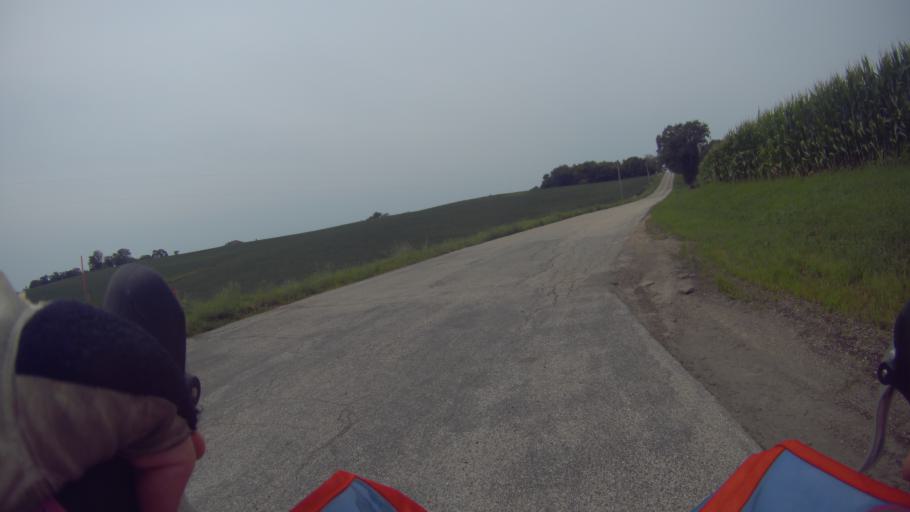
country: US
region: Wisconsin
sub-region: Dane County
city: Mount Horeb
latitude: 42.9846
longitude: -89.6620
